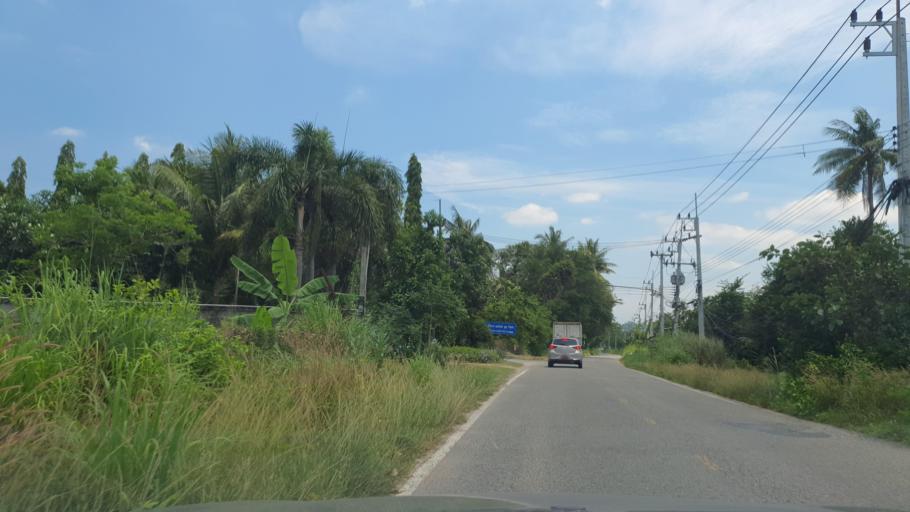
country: TH
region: Rayong
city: Ban Chang
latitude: 12.8087
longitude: 100.9460
